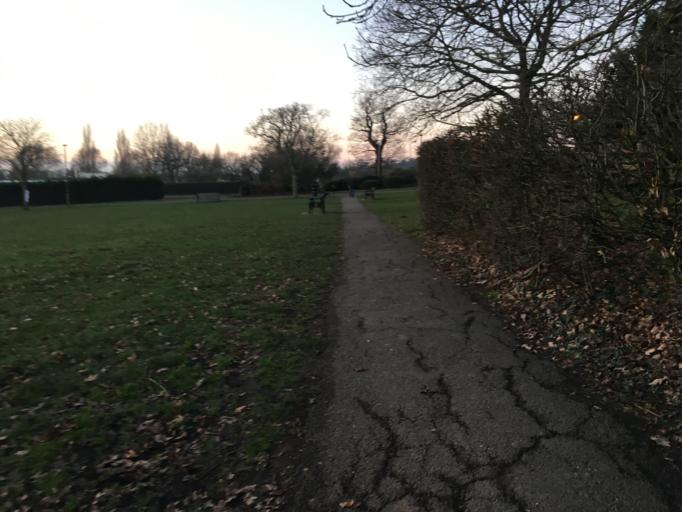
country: GB
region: England
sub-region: Greater London
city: Hendon
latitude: 51.6133
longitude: -0.2374
